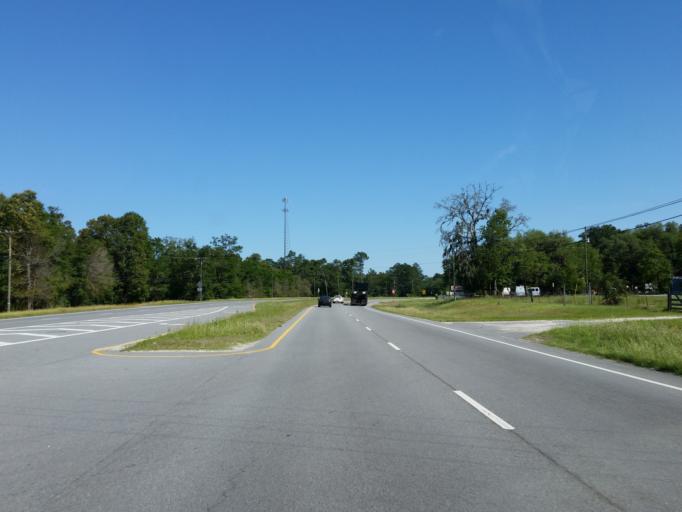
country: US
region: Georgia
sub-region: Lowndes County
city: Valdosta
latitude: 30.7915
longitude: -83.2374
